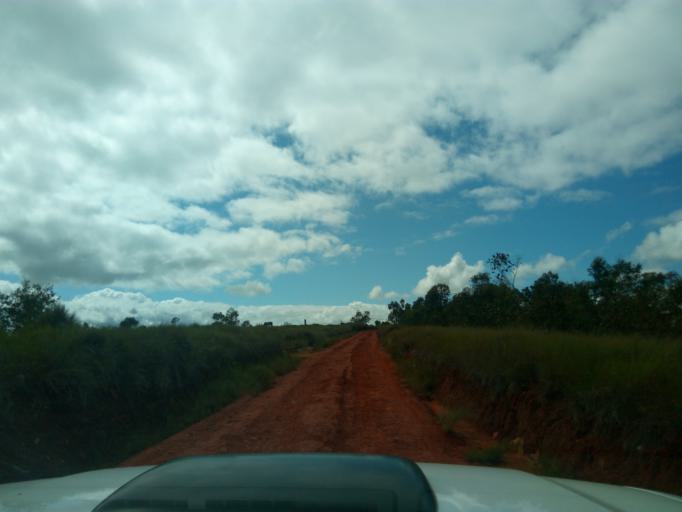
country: MG
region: Analamanga
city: Antananarivo
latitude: -18.7283
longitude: 47.4109
